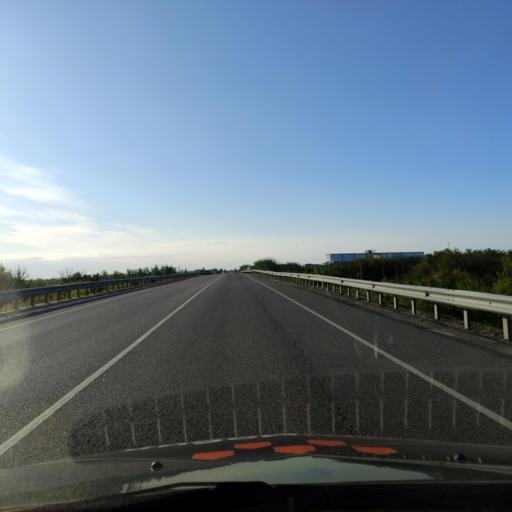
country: RU
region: Lipetsk
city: Yelets
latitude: 52.5643
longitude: 38.6773
